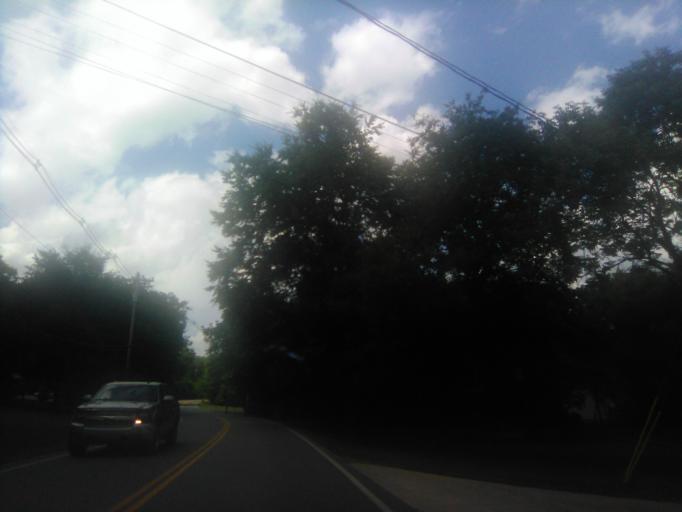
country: US
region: Tennessee
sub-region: Davidson County
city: Belle Meade
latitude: 36.1028
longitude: -86.8450
